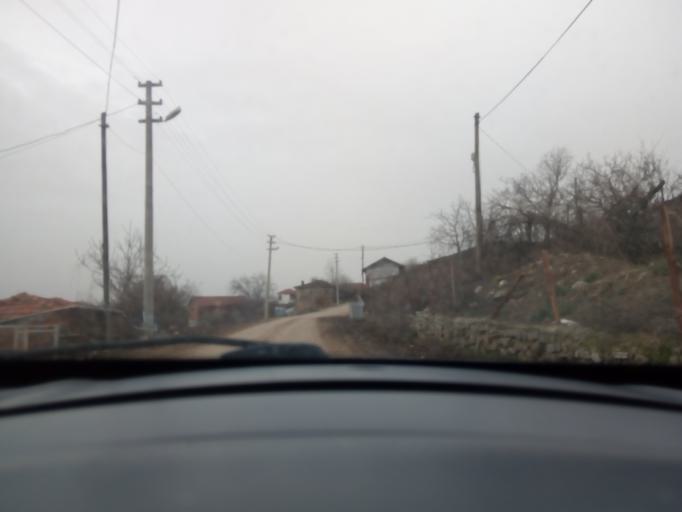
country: TR
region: Balikesir
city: Susurluk
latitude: 39.9169
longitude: 28.0898
